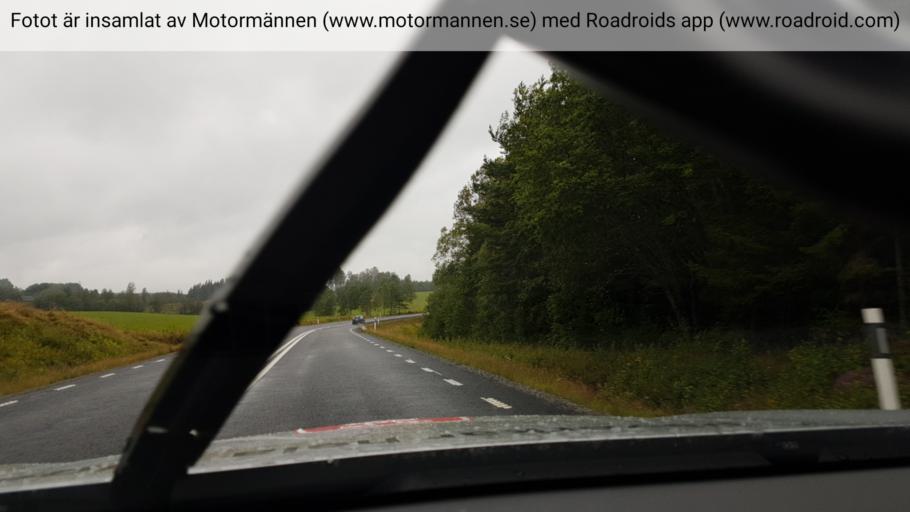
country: SE
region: Vaestra Goetaland
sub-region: Dals-Ed Kommun
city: Ed
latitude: 58.9037
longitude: 11.9913
